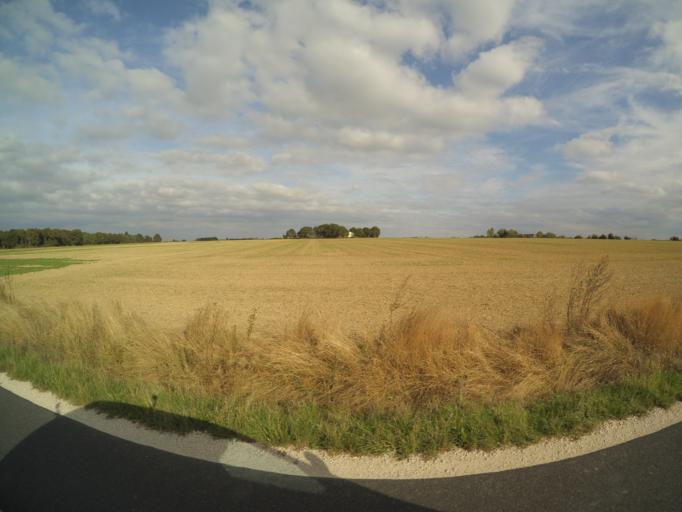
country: FR
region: Centre
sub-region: Departement d'Indre-et-Loire
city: Nazelles-Negron
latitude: 47.4507
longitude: 0.9560
